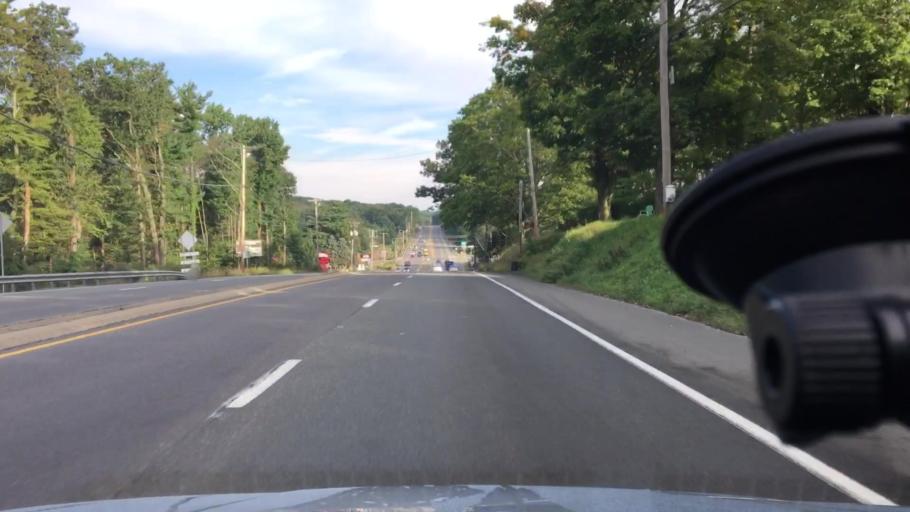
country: US
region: Pennsylvania
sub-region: Monroe County
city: Mount Pocono
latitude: 41.0988
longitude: -75.3330
